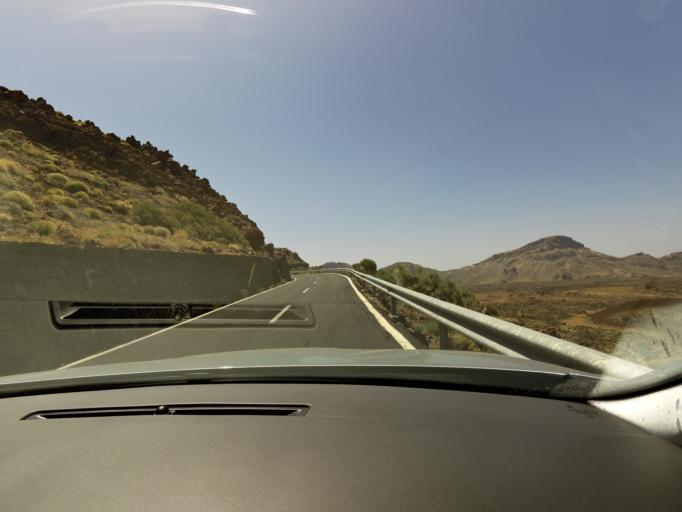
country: ES
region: Canary Islands
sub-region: Provincia de Santa Cruz de Tenerife
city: Vilaflor
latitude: 28.2593
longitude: -16.6139
